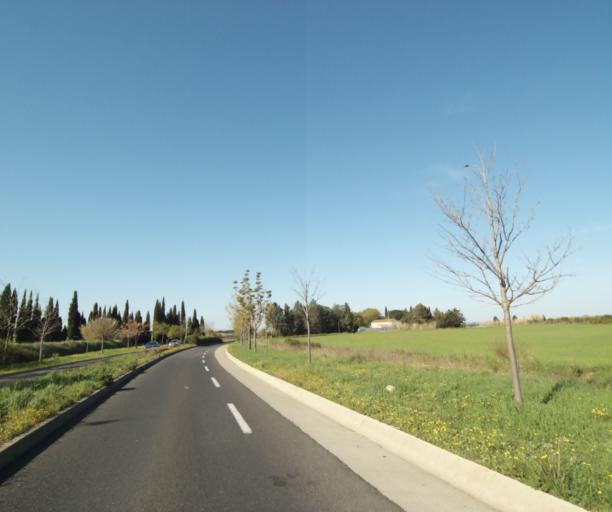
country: FR
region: Languedoc-Roussillon
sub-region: Departement de l'Herault
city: Le Cres
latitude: 43.6299
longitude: 3.9324
